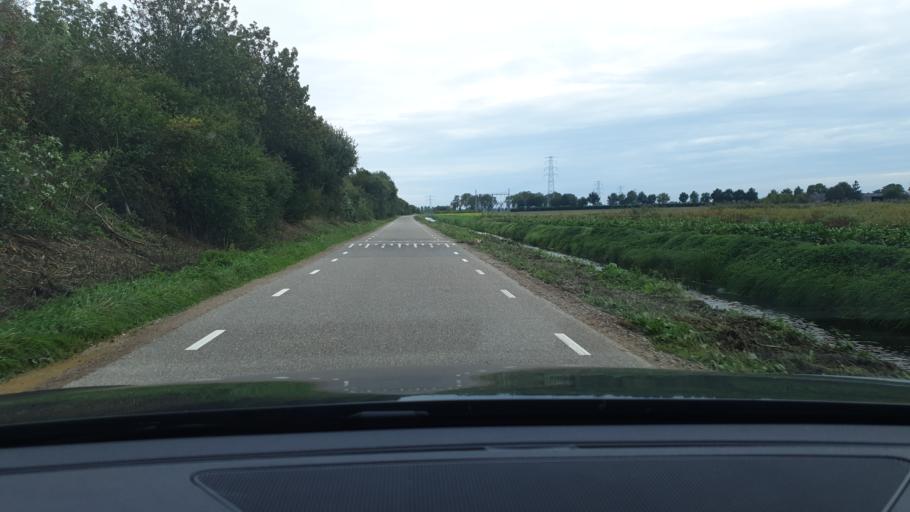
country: NL
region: Gelderland
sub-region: Gemeente Overbetuwe
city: Valburg
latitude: 51.8978
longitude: 5.8041
